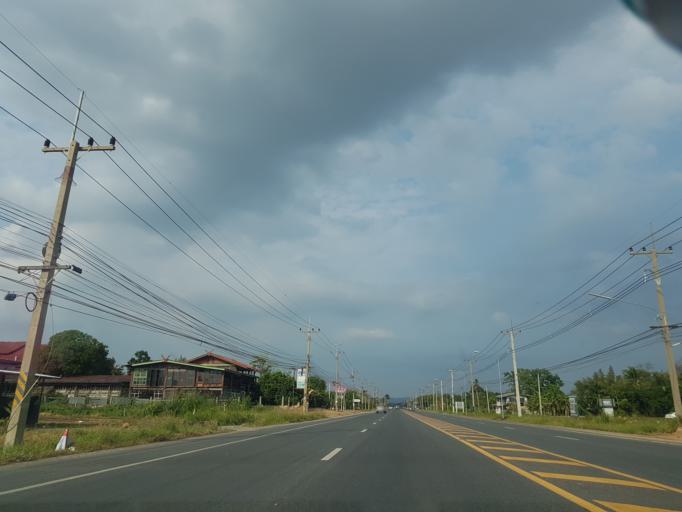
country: TH
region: Sara Buri
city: Phra Phutthabat
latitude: 14.6965
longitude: 100.7786
